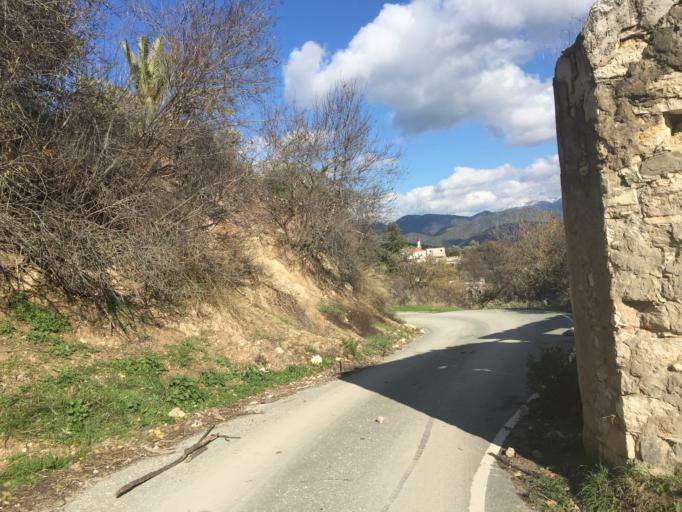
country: CY
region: Limassol
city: Pachna
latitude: 34.8909
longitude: 32.6564
